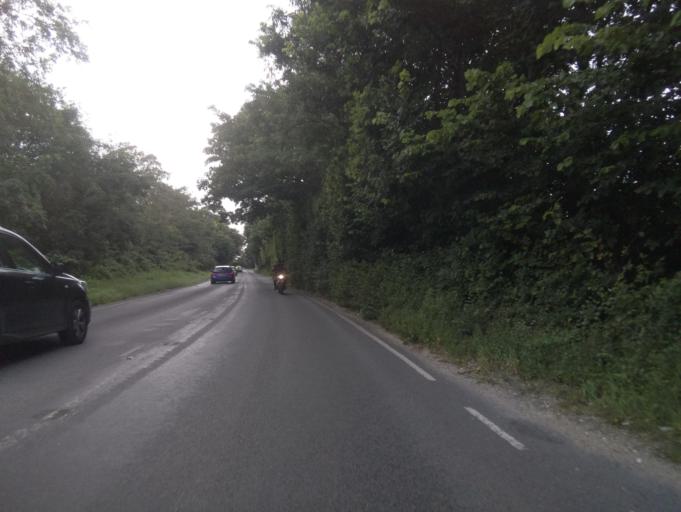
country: GB
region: England
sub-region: Hampshire
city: Milford on Sea
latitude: 50.7450
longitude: -1.5806
